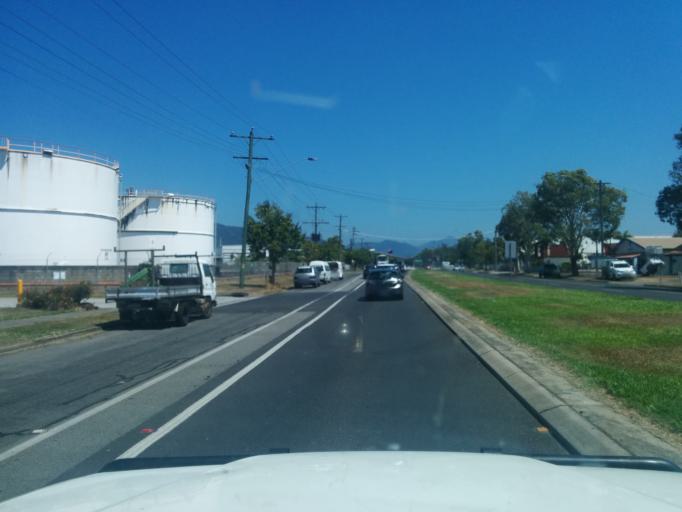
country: AU
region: Queensland
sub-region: Cairns
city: Cairns
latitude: -16.9336
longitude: 145.7747
